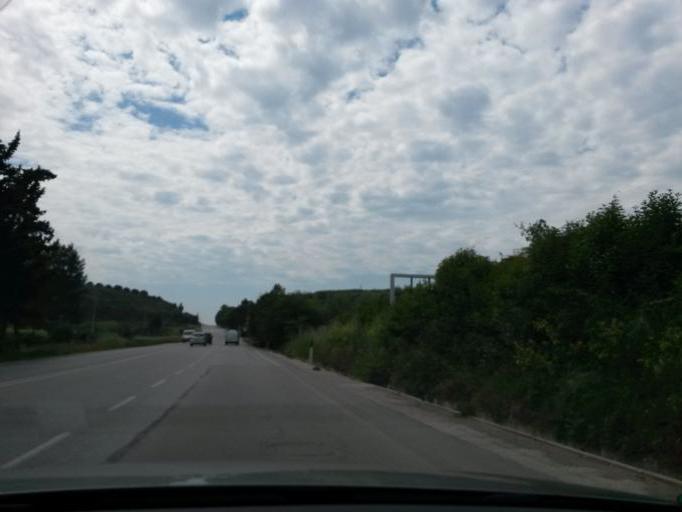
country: IT
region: Tuscany
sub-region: Provincia di Livorno
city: Piombino
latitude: 42.9598
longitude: 10.5373
